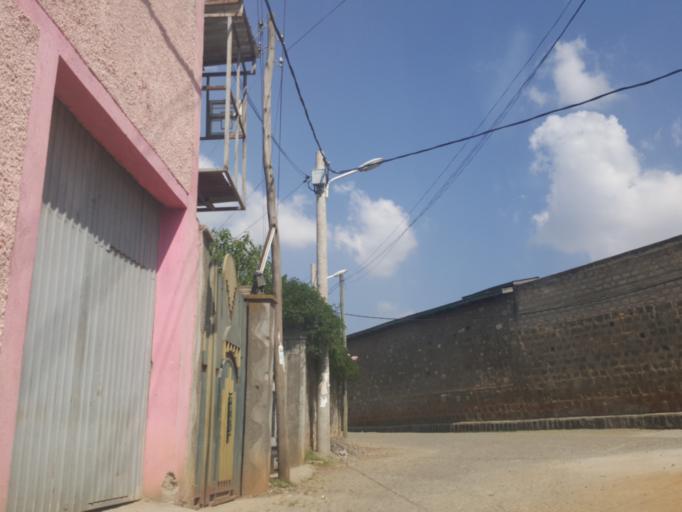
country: ET
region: Adis Abeba
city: Addis Ababa
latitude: 9.0550
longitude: 38.7300
